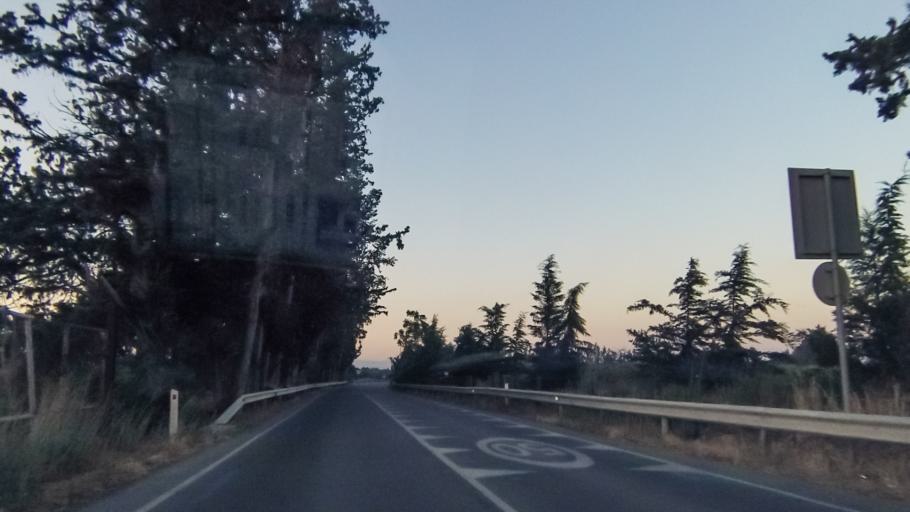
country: CY
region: Larnaka
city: Kolossi
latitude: 34.6405
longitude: 32.9630
